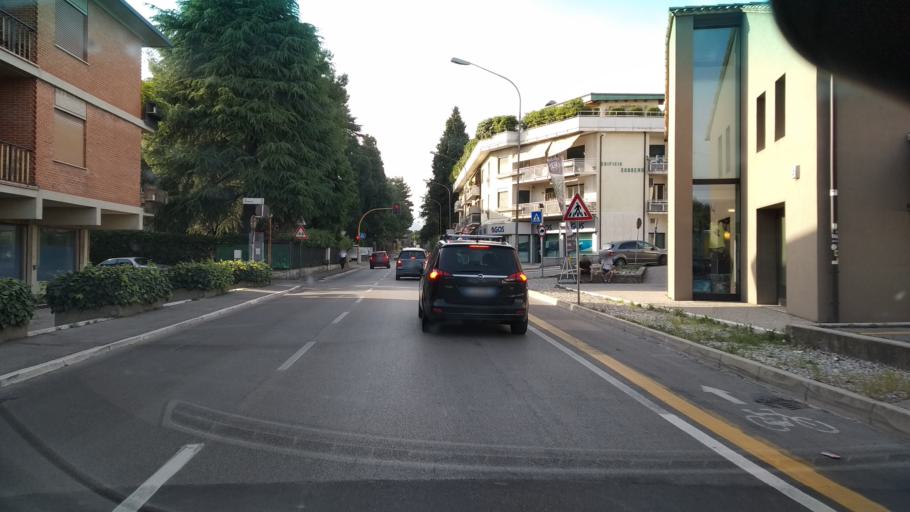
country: IT
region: Veneto
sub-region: Provincia di Vicenza
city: Bassano del Grappa
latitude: 45.7625
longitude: 11.7402
